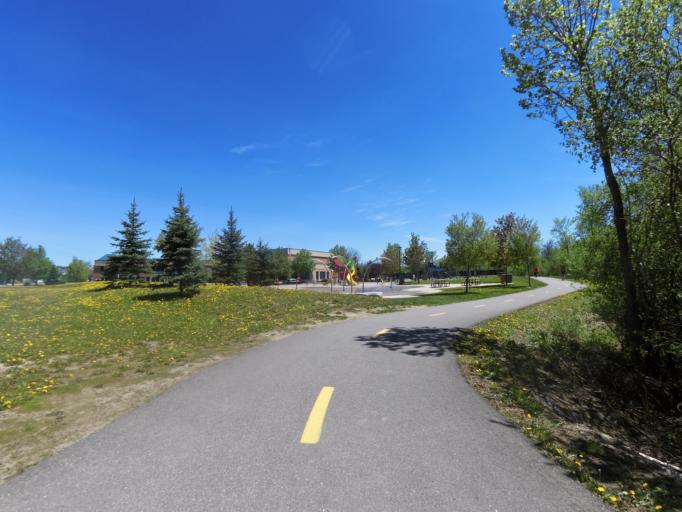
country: CA
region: Ontario
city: Ottawa
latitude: 45.4394
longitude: -75.7833
